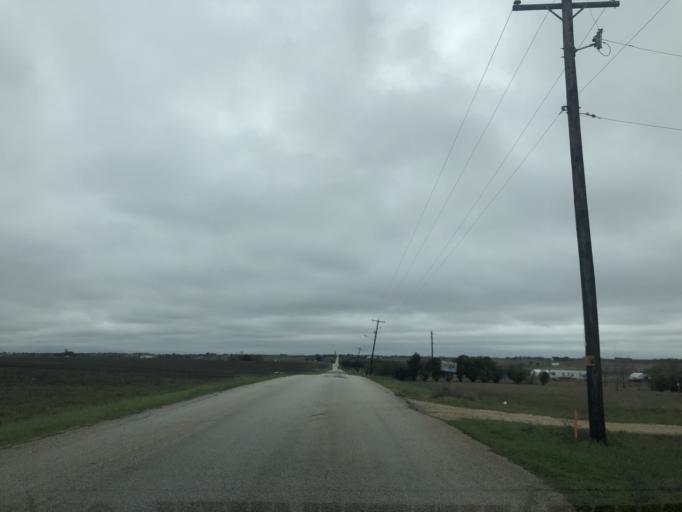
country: US
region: Texas
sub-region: Williamson County
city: Hutto
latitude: 30.5972
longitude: -97.5032
